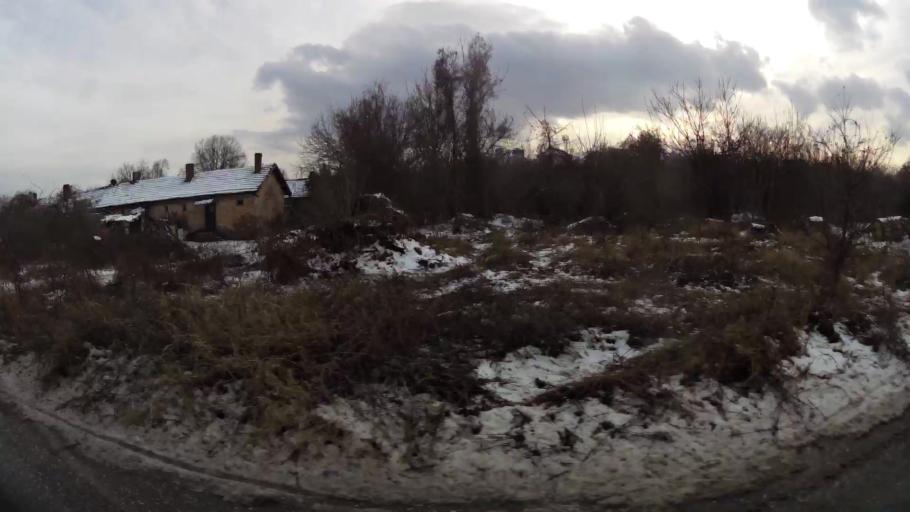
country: BG
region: Sofia-Capital
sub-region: Stolichna Obshtina
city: Sofia
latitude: 42.6973
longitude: 23.3656
